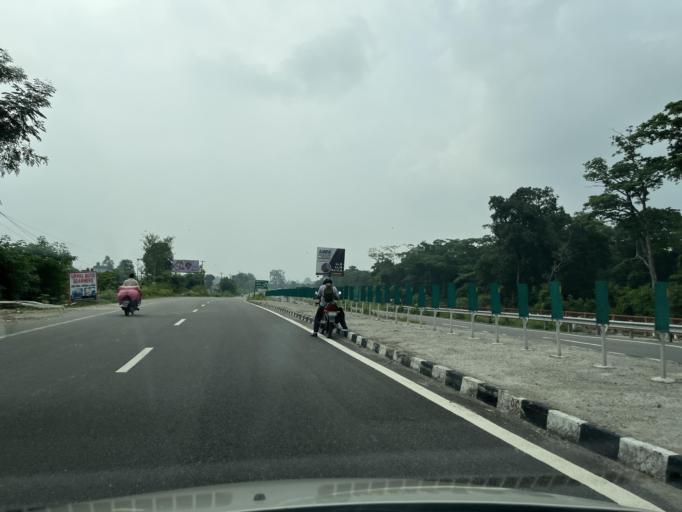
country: IN
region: Uttarakhand
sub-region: Dehradun
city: Raiwala
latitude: 30.0625
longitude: 78.2115
